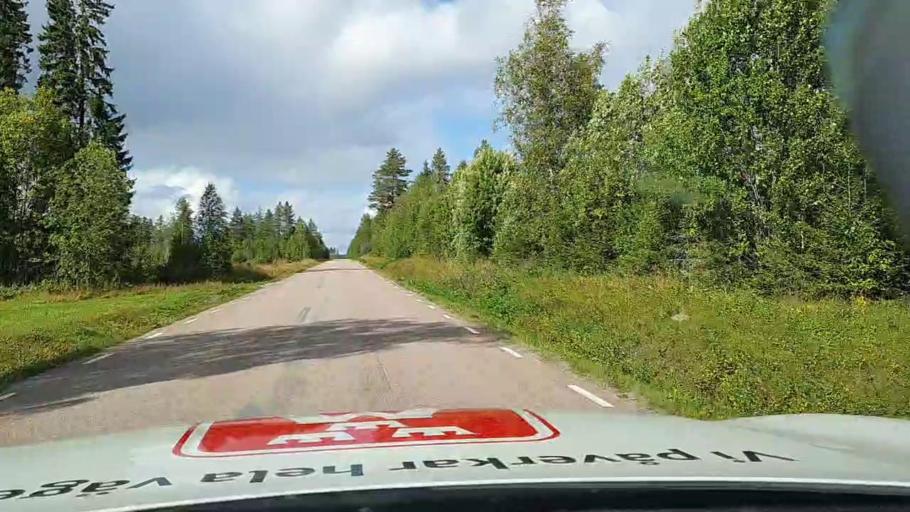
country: SE
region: Jaemtland
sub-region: Stroemsunds Kommun
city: Stroemsund
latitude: 63.8488
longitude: 15.4013
